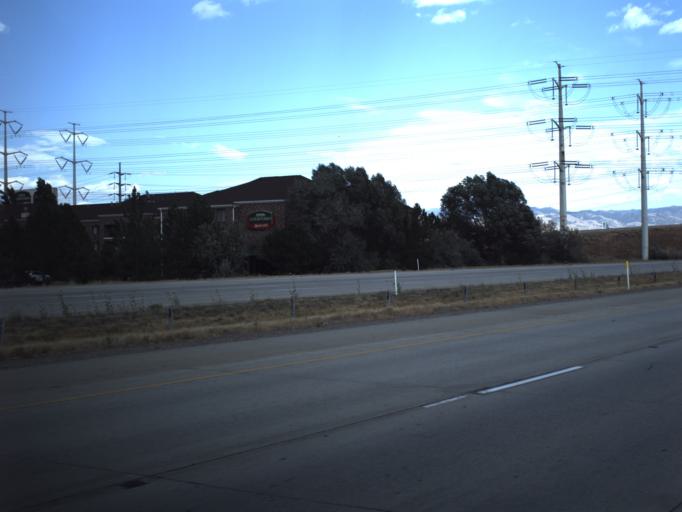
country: US
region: Utah
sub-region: Salt Lake County
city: West Valley City
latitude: 40.7702
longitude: -112.0084
